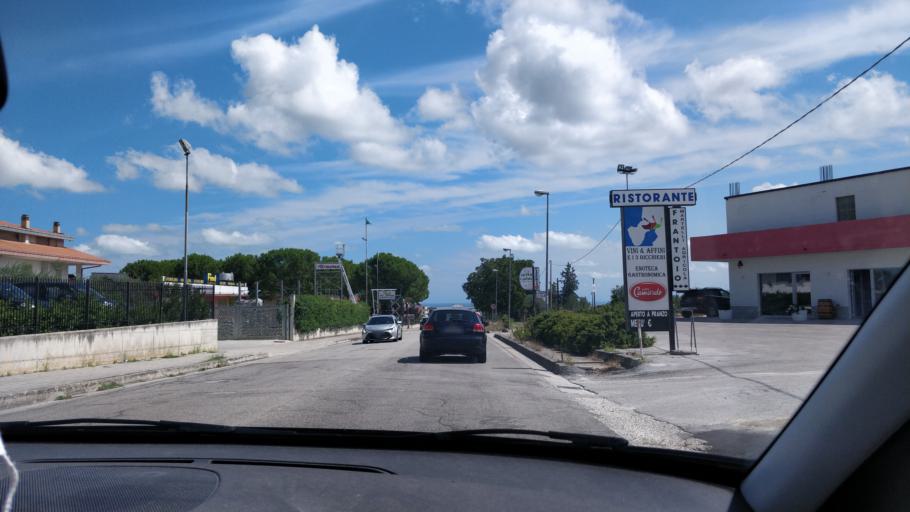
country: IT
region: Abruzzo
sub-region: Provincia di Chieti
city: Treglio
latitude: 42.2500
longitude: 14.4233
